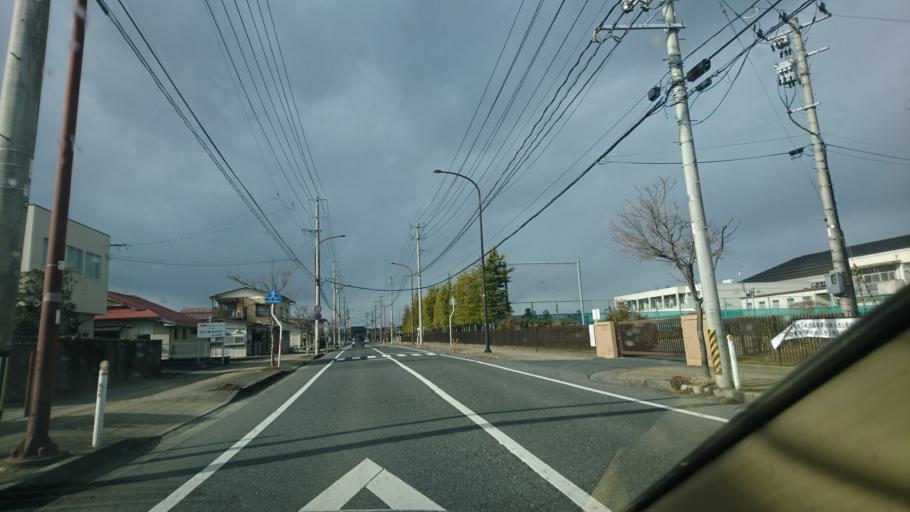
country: JP
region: Miyagi
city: Tomiya
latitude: 38.4410
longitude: 140.9037
